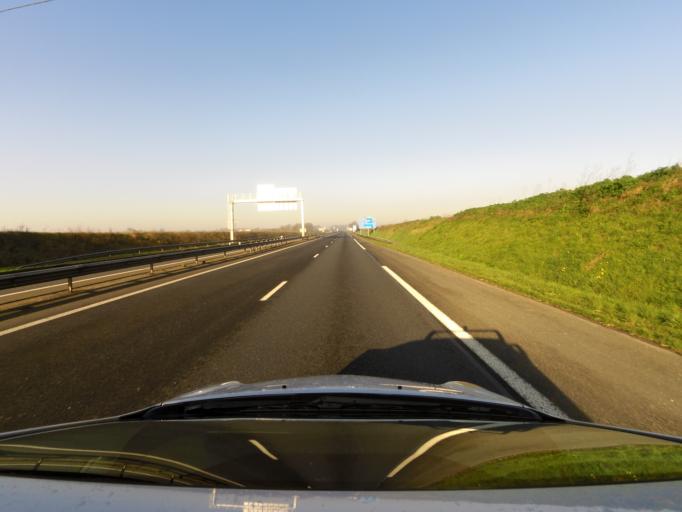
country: FR
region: Lower Normandy
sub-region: Departement du Calvados
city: Bretteville-sur-Odon
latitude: 49.1645
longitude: -0.4362
